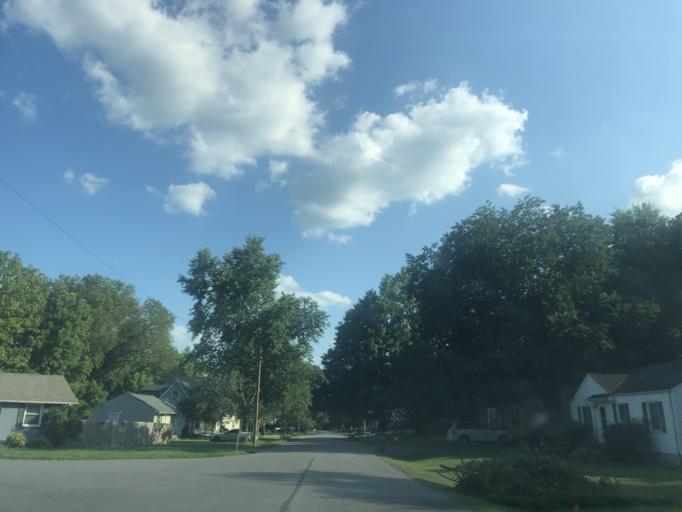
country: US
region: Tennessee
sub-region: Davidson County
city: Nashville
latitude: 36.1692
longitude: -86.7460
